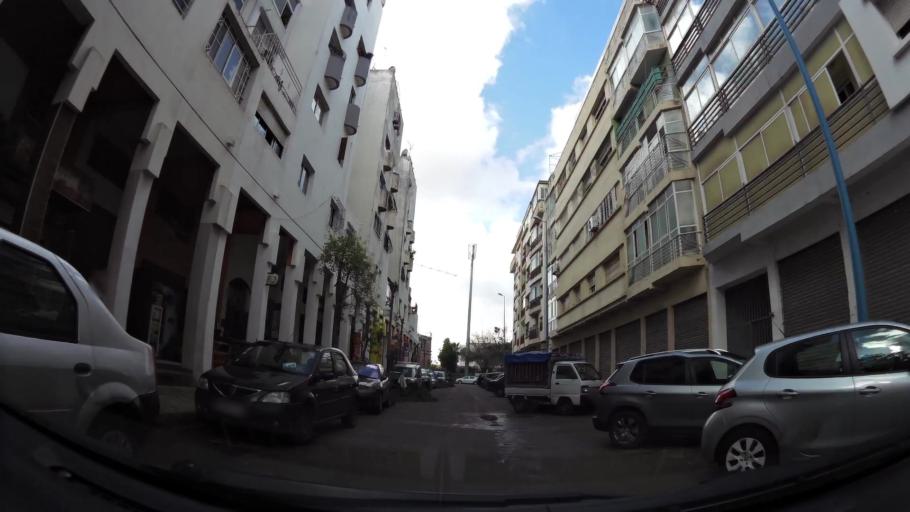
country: MA
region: Grand Casablanca
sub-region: Casablanca
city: Casablanca
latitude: 33.5556
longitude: -7.6287
